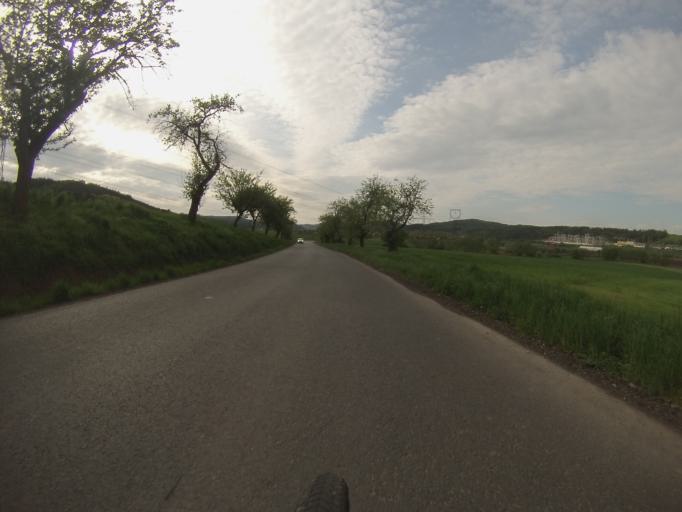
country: CZ
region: South Moravian
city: Cebin
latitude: 49.3199
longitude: 16.4564
